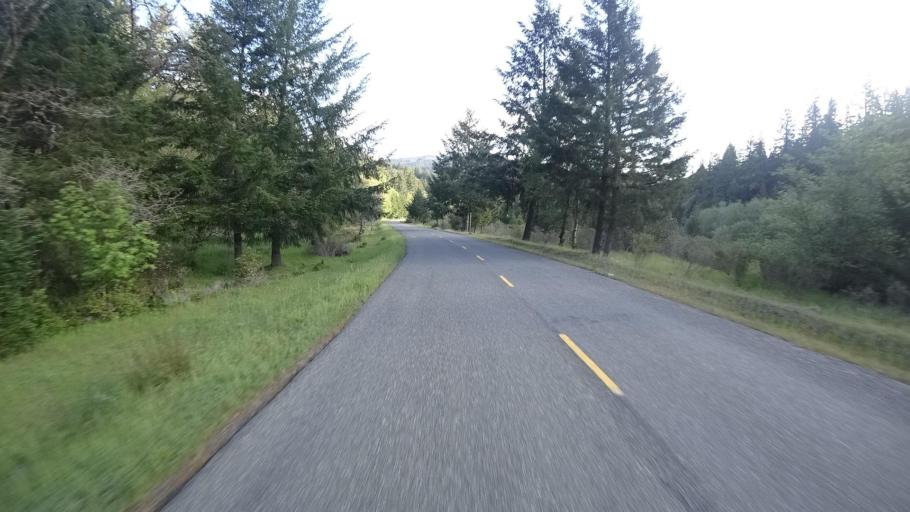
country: US
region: California
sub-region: Humboldt County
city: Rio Dell
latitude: 40.3406
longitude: -124.0265
